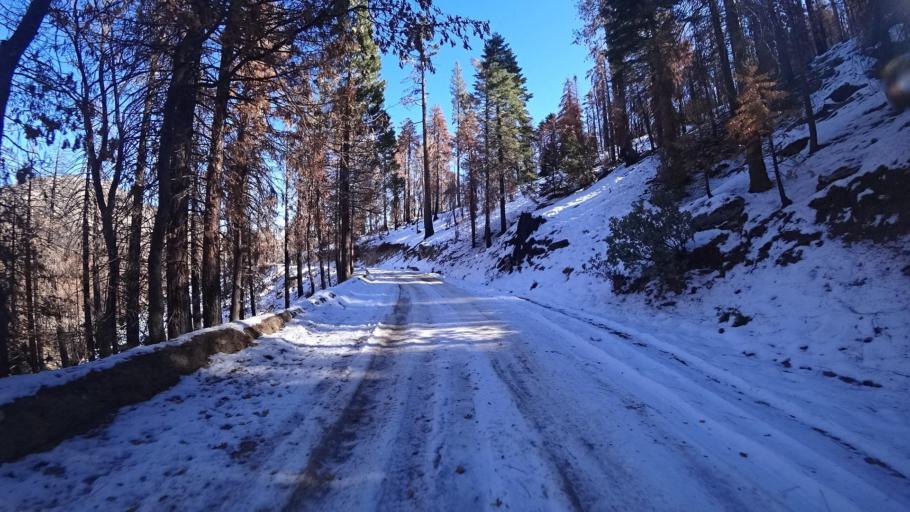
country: US
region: California
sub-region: Kern County
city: Alta Sierra
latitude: 35.7162
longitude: -118.5430
